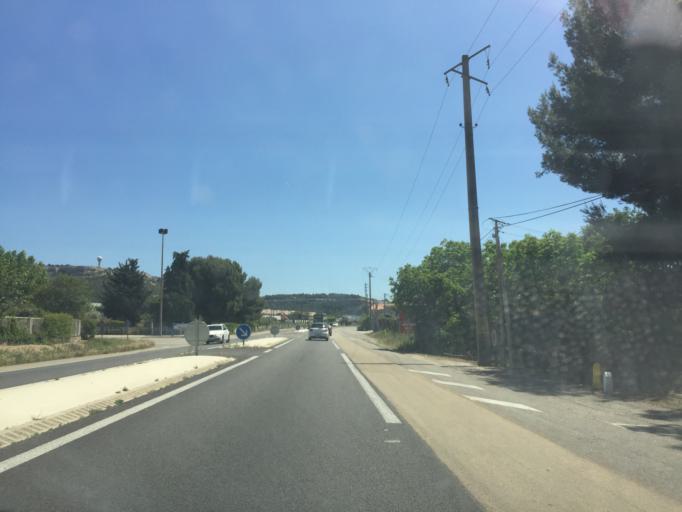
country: FR
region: Provence-Alpes-Cote d'Azur
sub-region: Departement des Bouches-du-Rhone
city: Rognac
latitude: 43.4805
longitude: 5.2261
